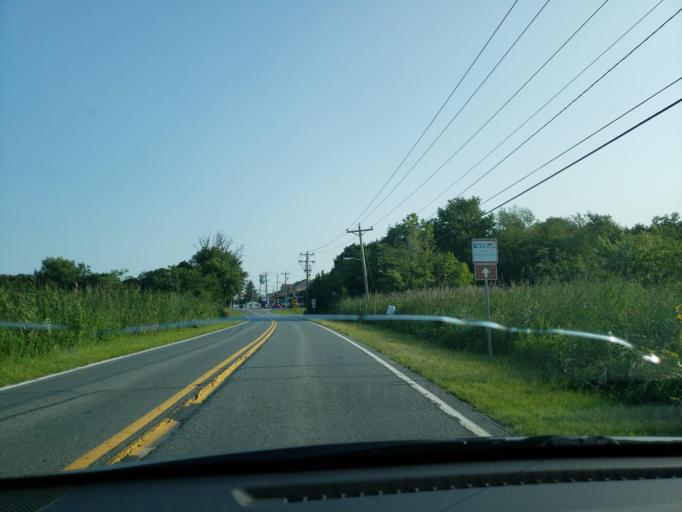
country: US
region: Delaware
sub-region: Kent County
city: Riverview
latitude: 39.0111
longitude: -75.4647
